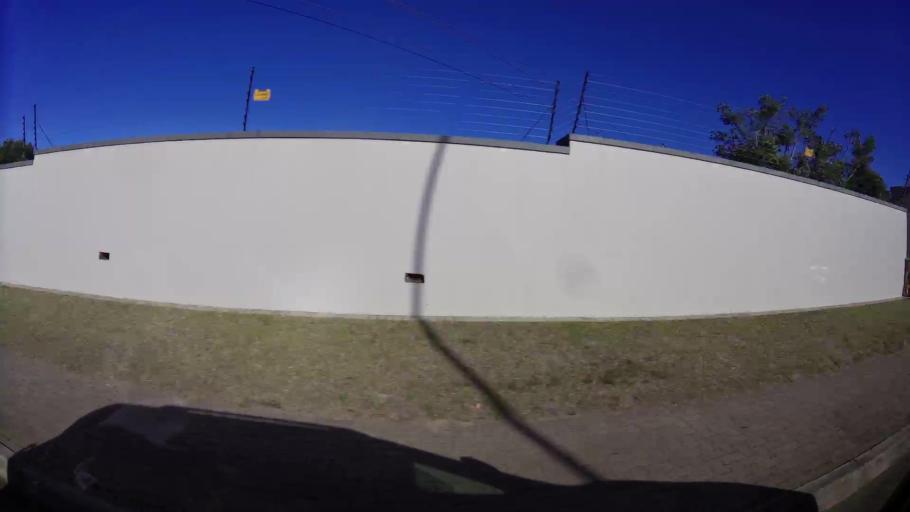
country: ZA
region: Western Cape
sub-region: Eden District Municipality
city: George
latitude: -33.9648
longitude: 22.4298
